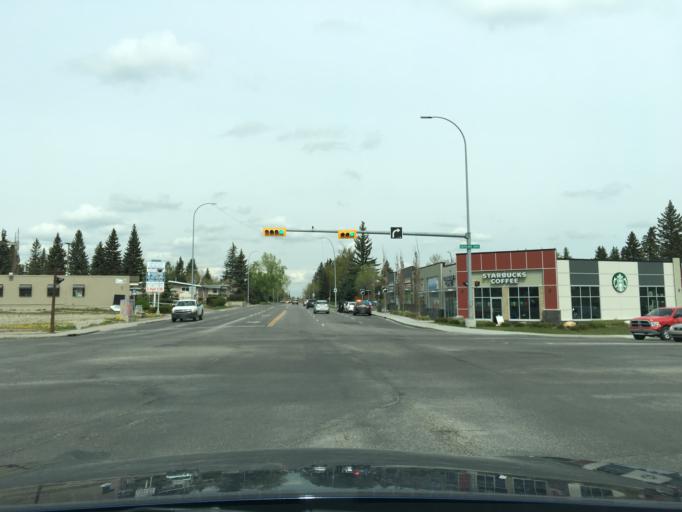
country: CA
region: Alberta
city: Calgary
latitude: 50.9634
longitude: -114.0848
